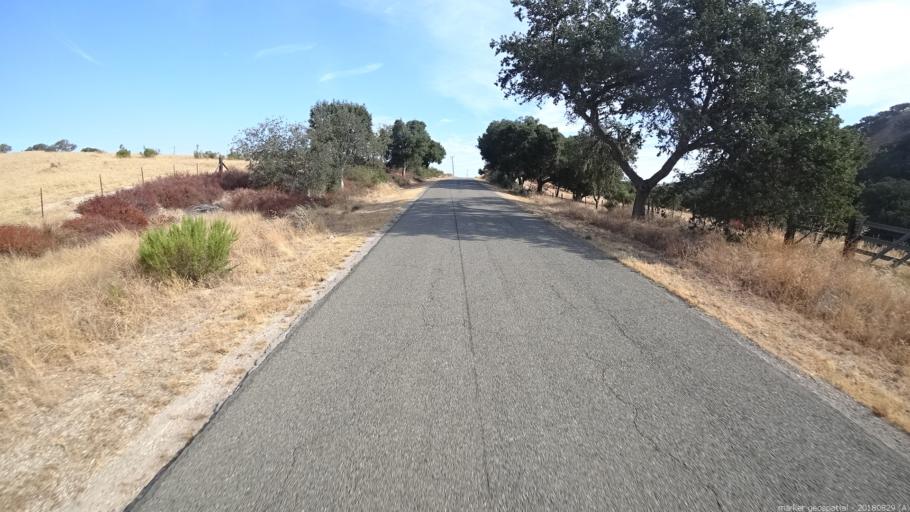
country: US
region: California
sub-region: Monterey County
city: King City
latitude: 36.0647
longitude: -121.0412
